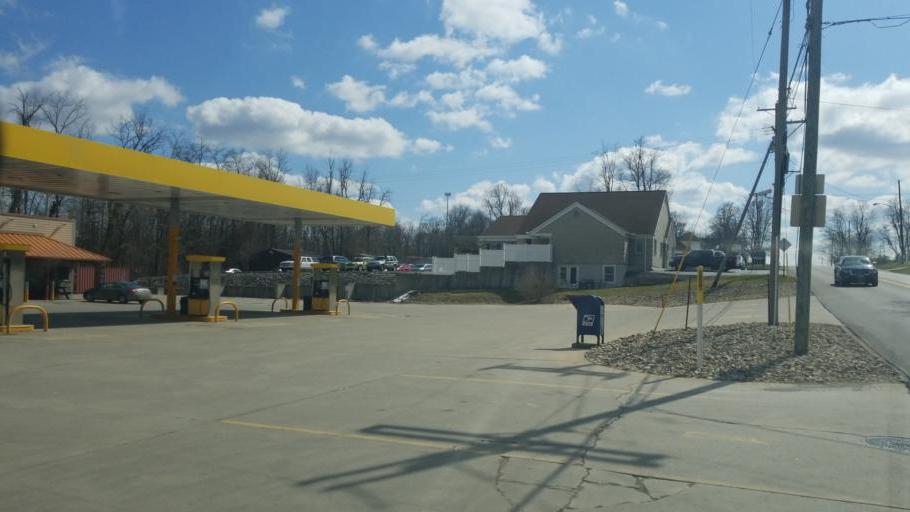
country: US
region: Ohio
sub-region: Highland County
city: Hillsboro
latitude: 39.1962
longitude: -83.6128
